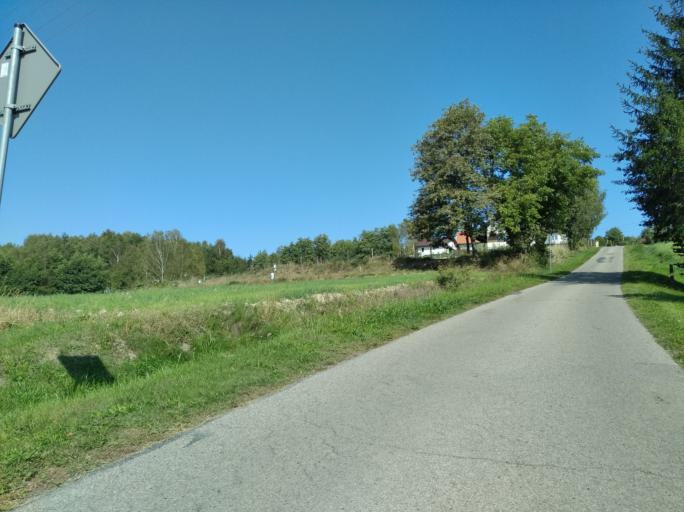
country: PL
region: Subcarpathian Voivodeship
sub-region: Powiat strzyzowski
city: Czudec
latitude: 49.9651
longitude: 21.8098
